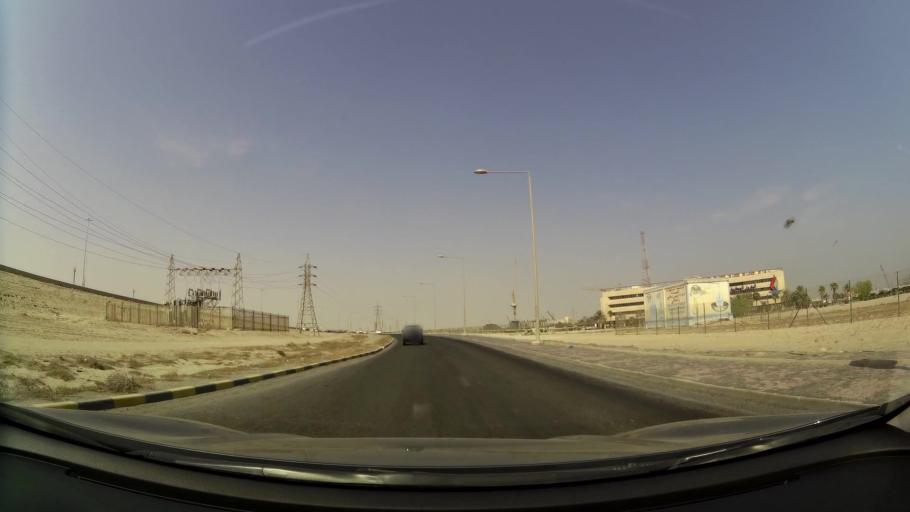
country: KW
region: Al Ahmadi
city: Al Fahahil
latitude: 28.9985
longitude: 48.1421
